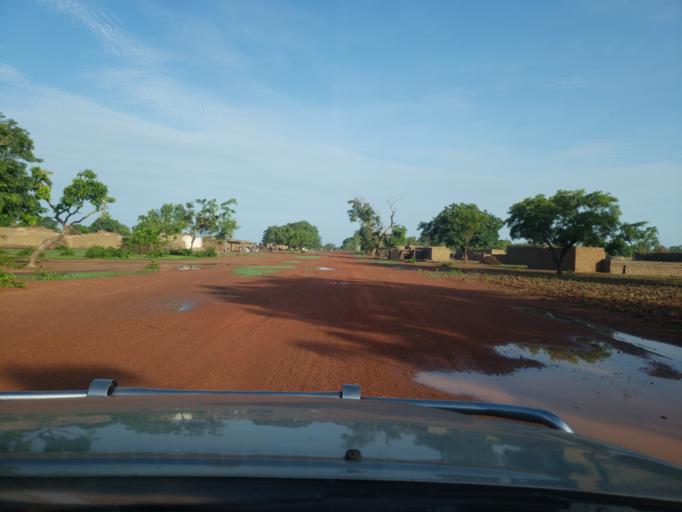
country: ML
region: Sikasso
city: Koutiala
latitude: 12.4183
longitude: -5.5762
